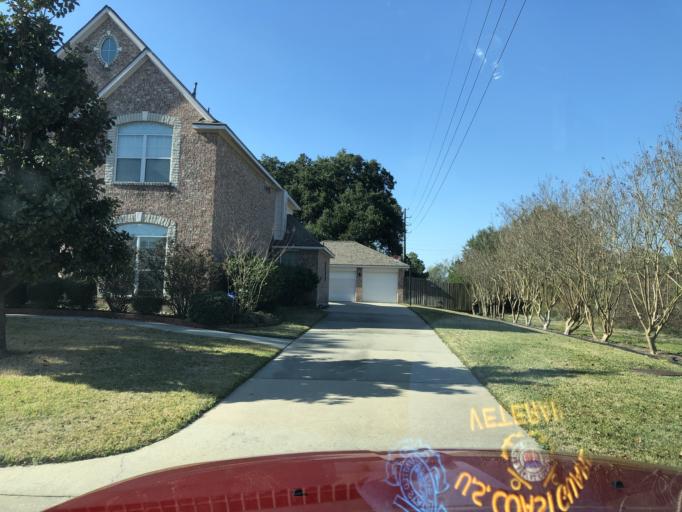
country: US
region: Texas
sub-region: Harris County
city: Tomball
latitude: 30.0377
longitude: -95.5466
